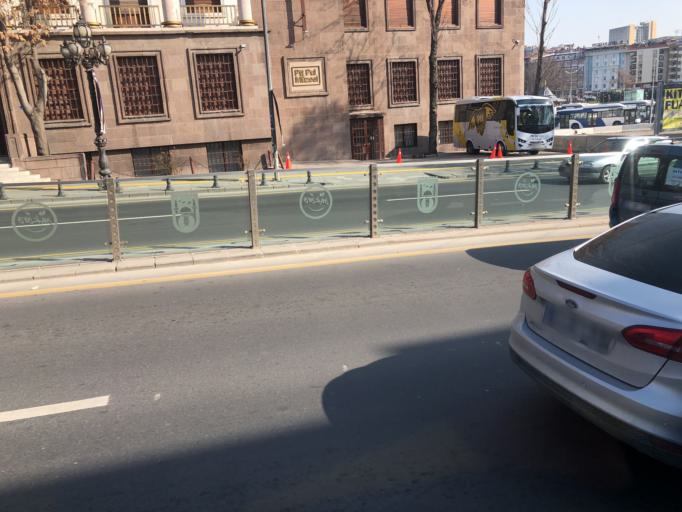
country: TR
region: Ankara
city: Ankara
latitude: 39.9383
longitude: 32.8544
